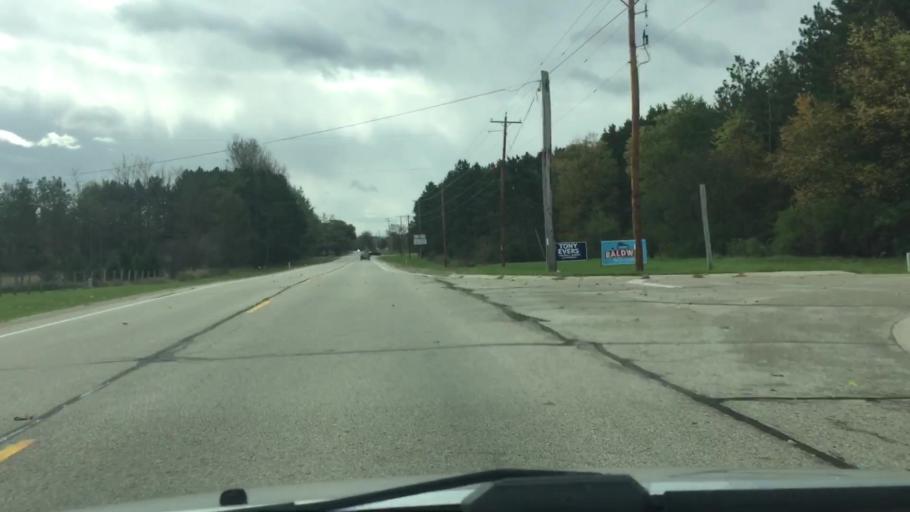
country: US
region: Wisconsin
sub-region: Waukesha County
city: Dousman
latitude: 42.9560
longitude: -88.4786
